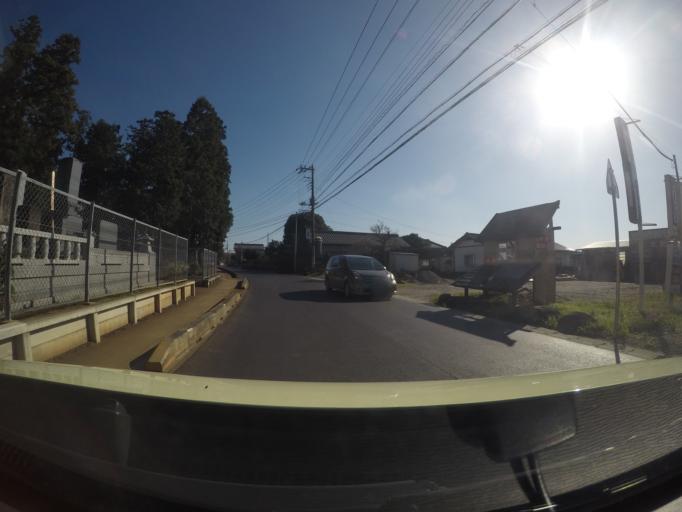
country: JP
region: Ibaraki
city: Naka
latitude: 36.0974
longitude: 140.1250
